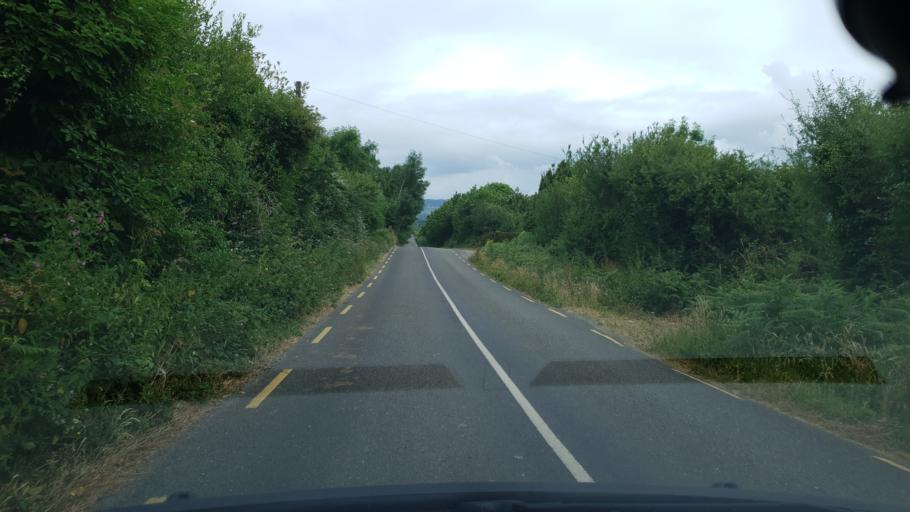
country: IE
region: Munster
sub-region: Ciarrai
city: Cill Airne
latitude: 52.1586
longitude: -9.6019
